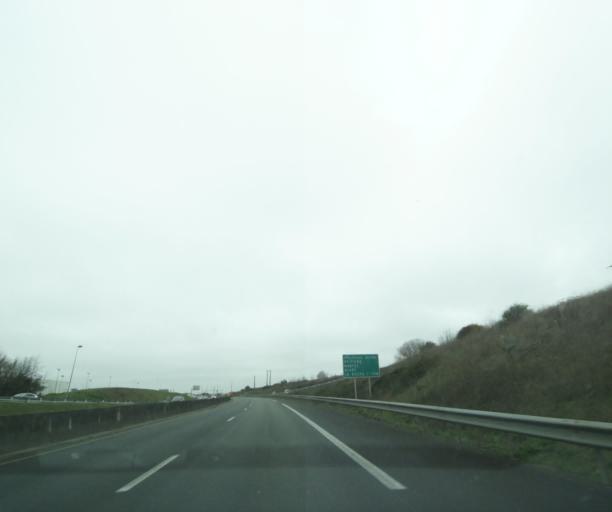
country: FR
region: Poitou-Charentes
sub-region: Departement de la Charente-Maritime
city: Perigny
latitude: 46.1537
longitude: -1.1140
